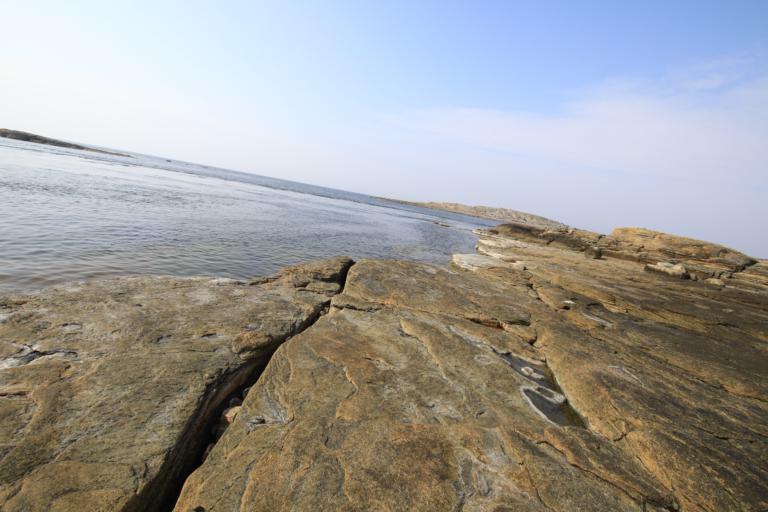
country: SE
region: Halland
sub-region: Kungsbacka Kommun
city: Frillesas
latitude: 57.2521
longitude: 12.0908
